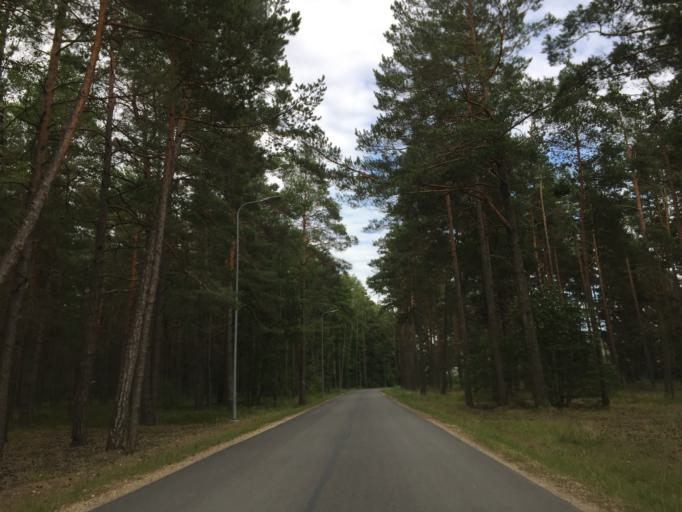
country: LV
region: Carnikava
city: Carnikava
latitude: 57.1351
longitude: 24.2486
